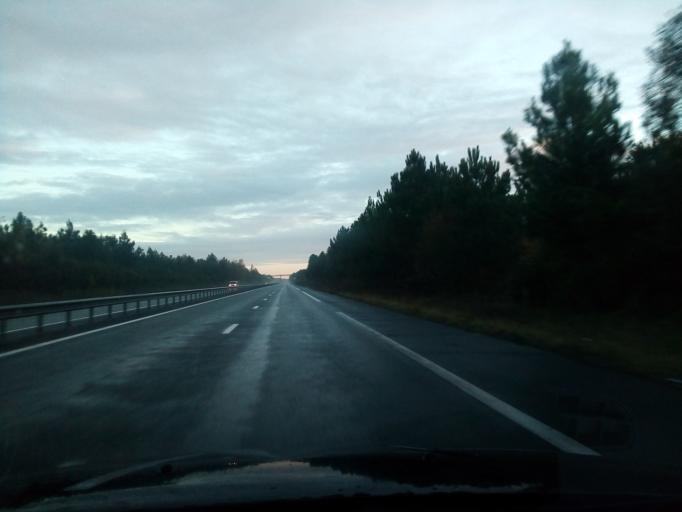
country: FR
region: Aquitaine
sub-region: Departement de la Gironde
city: Saint-Mariens
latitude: 45.1322
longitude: -0.3716
